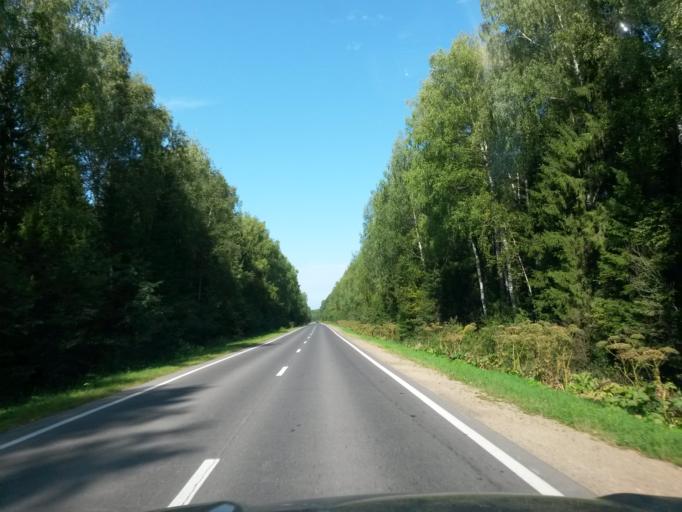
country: RU
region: Jaroslavl
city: Yaroslavl
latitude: 57.8013
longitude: 39.7933
